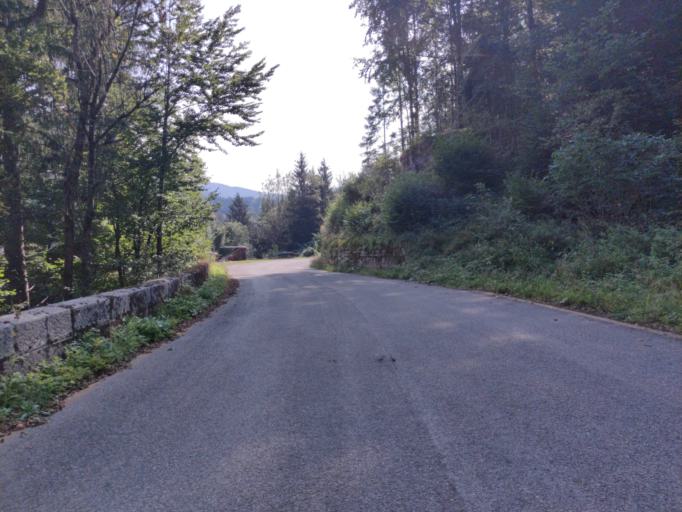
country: IT
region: Friuli Venezia Giulia
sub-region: Provincia di Udine
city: Tarvisio
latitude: 46.5183
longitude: 13.6127
